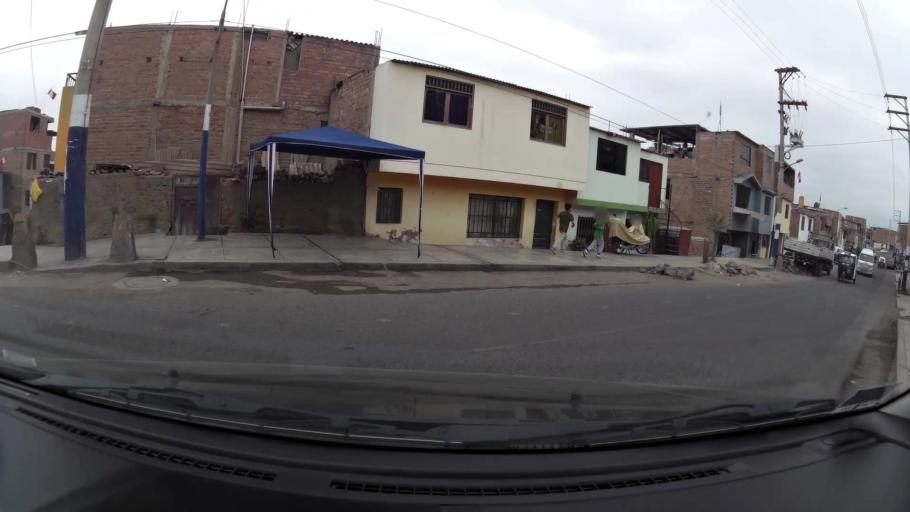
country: PE
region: Lima
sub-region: Lima
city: Surco
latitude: -12.1877
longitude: -76.9902
